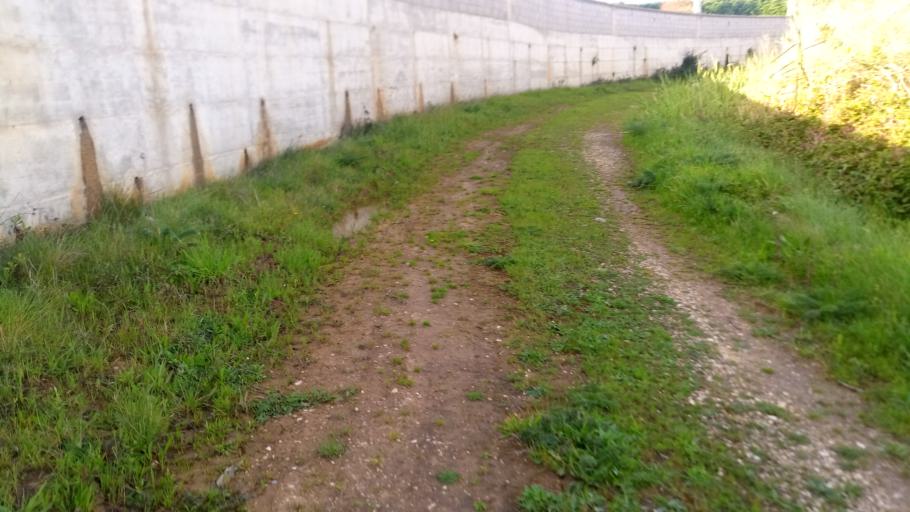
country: PT
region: Leiria
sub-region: Caldas da Rainha
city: Caldas da Rainha
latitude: 39.4552
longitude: -9.1992
